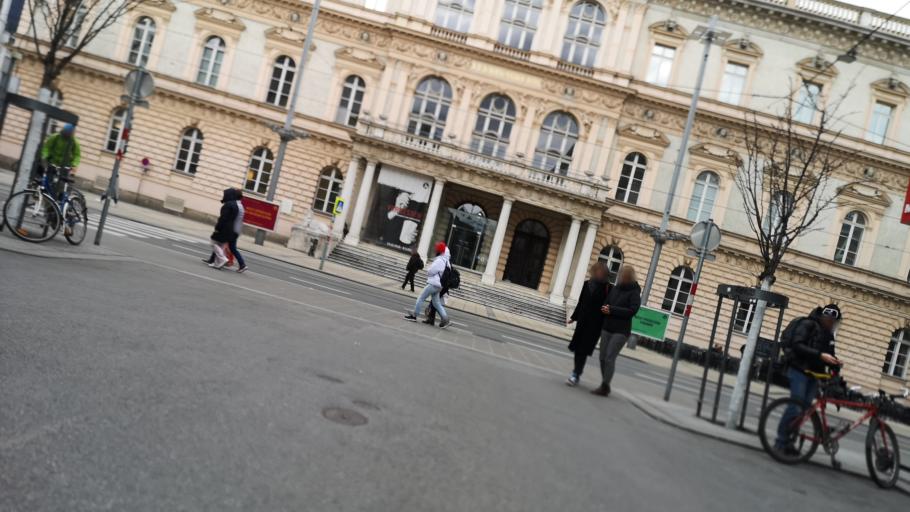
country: AT
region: Tyrol
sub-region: Innsbruck Stadt
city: Innsbruck
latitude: 47.2667
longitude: 11.3975
